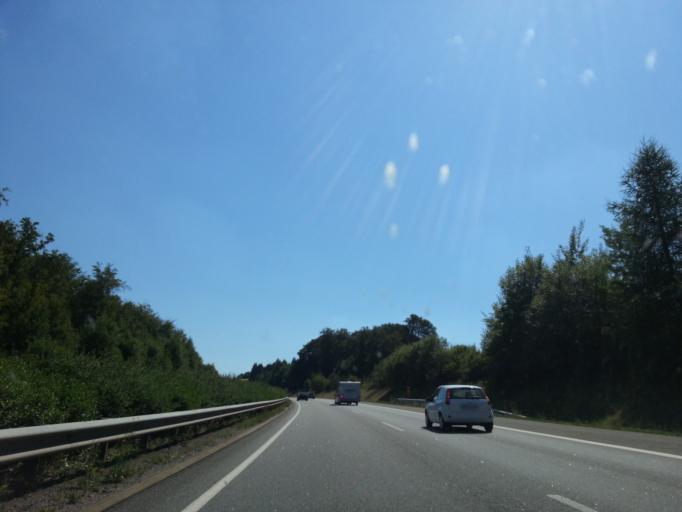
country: DE
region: Rheinland-Pfalz
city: Bergweiler
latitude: 49.9806
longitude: 6.7997
